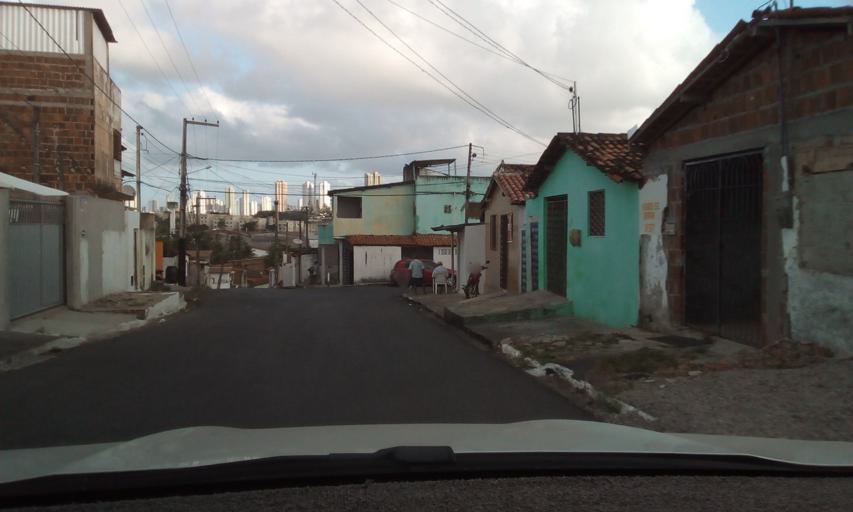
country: BR
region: Paraiba
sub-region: Joao Pessoa
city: Joao Pessoa
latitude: -7.0958
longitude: -34.8621
